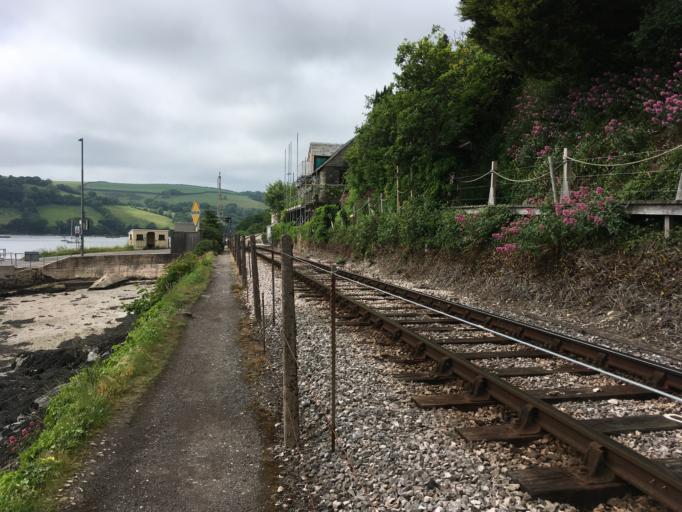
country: GB
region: England
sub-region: Devon
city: Dartmouth
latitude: 50.3595
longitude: -3.5726
